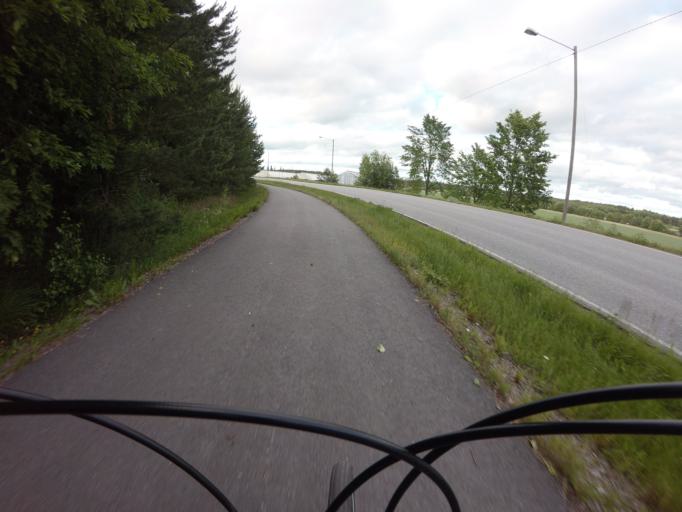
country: FI
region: Varsinais-Suomi
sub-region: Turku
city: Turku
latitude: 60.5012
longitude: 22.3328
